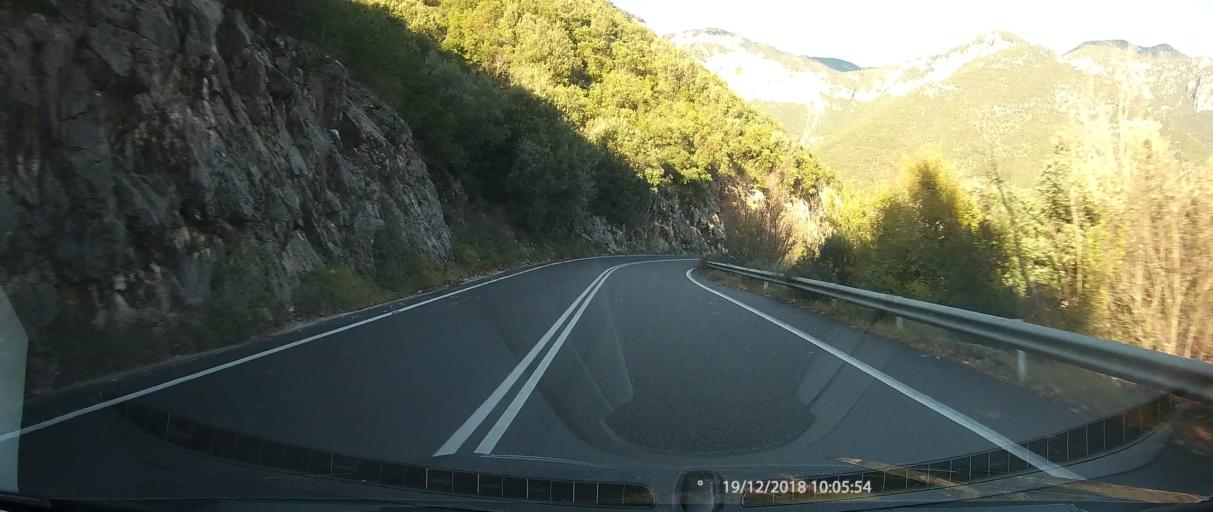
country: GR
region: Peloponnese
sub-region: Nomos Messinias
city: Paralia Vergas
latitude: 37.1122
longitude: 22.2122
